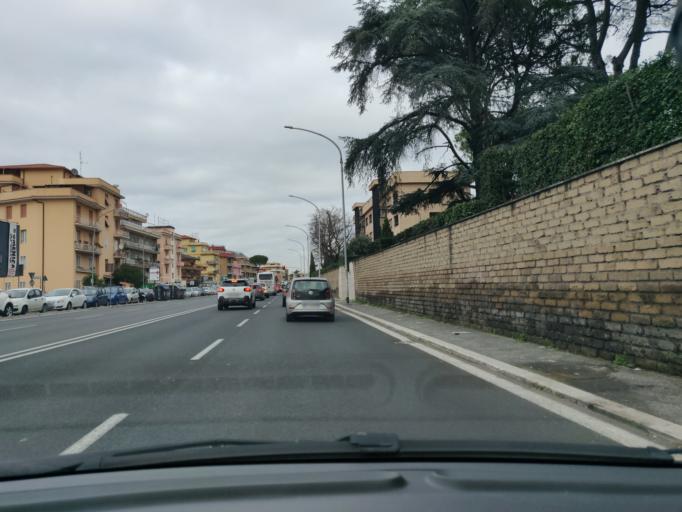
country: VA
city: Vatican City
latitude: 41.8932
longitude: 12.4151
